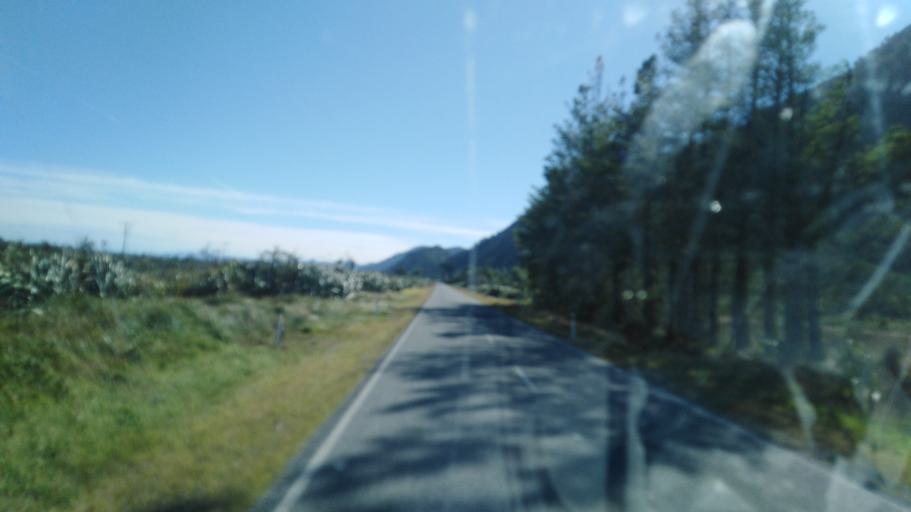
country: NZ
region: West Coast
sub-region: Buller District
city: Westport
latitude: -41.6441
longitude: 171.8392
